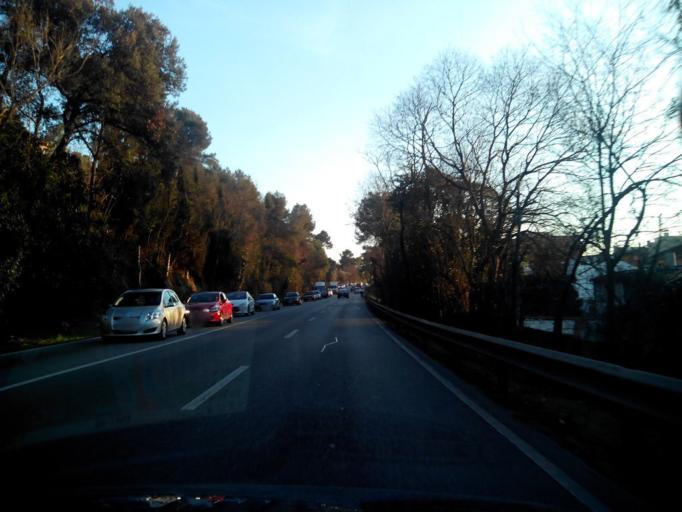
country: ES
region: Catalonia
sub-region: Provincia de Barcelona
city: Rubi
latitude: 41.5257
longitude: 2.0390
